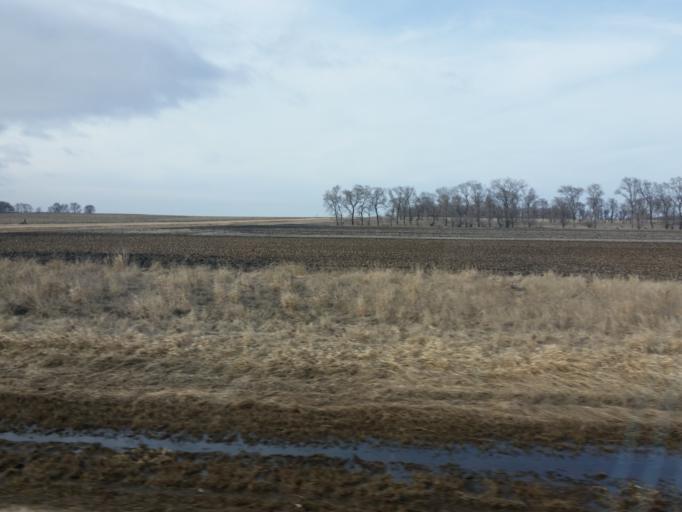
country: US
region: North Dakota
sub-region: Richland County
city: Wahpeton
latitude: 46.4712
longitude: -96.6553
